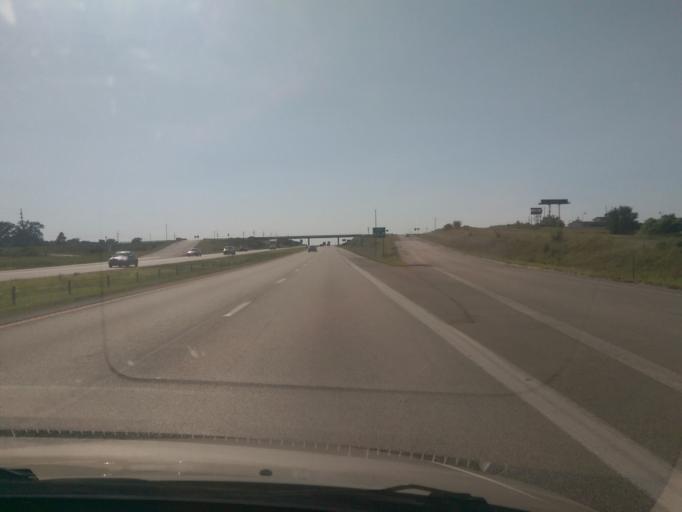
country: US
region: Missouri
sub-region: Saline County
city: Sweet Springs
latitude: 38.9840
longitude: -93.4900
